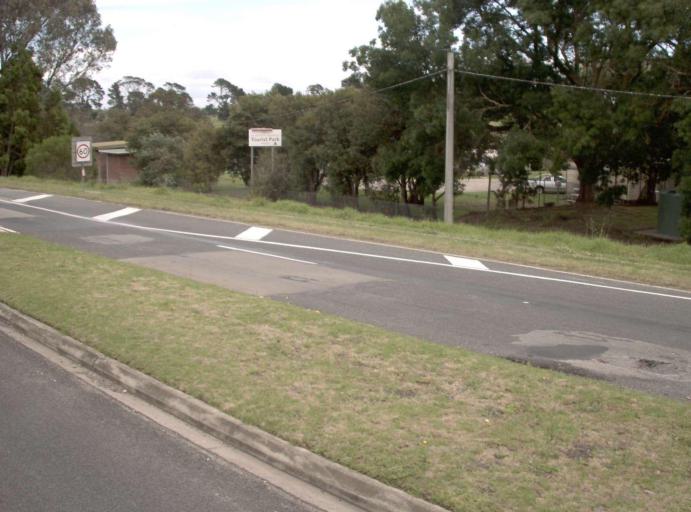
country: AU
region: Victoria
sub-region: Wellington
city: Sale
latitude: -37.9705
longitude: 147.0789
